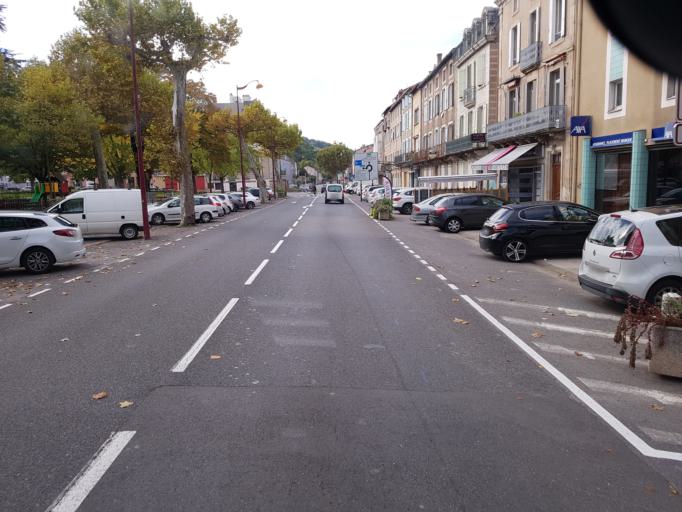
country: FR
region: Midi-Pyrenees
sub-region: Departement de l'Aveyron
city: Saint-Affrique
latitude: 43.9579
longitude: 2.8830
